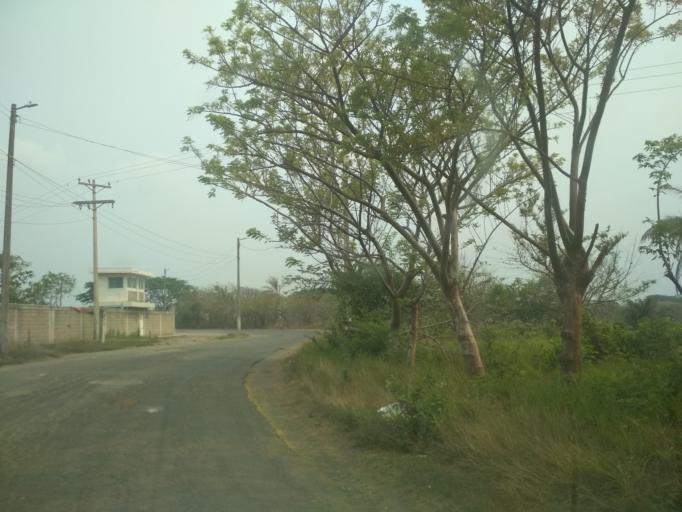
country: MX
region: Veracruz
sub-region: Veracruz
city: Delfino Victoria (Santa Fe)
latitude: 19.2102
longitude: -96.2579
